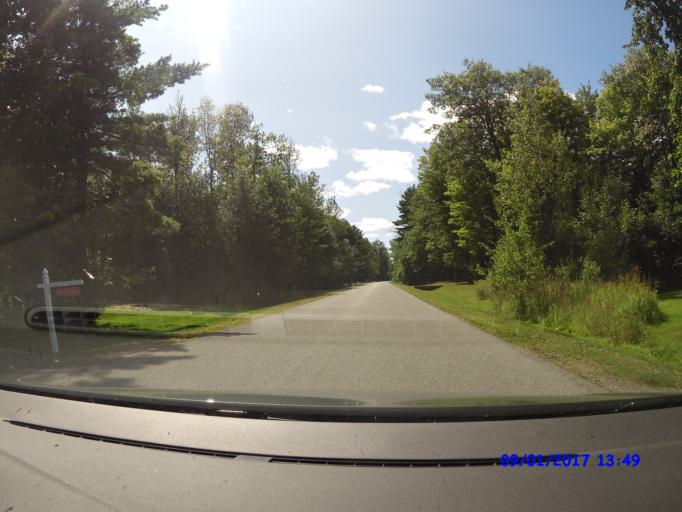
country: CA
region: Ontario
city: Bells Corners
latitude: 45.3685
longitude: -75.9669
